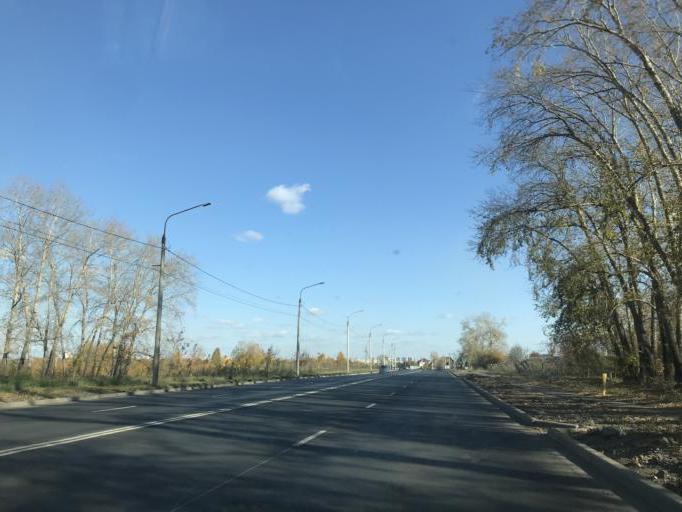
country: RU
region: Chelyabinsk
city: Roshchino
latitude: 55.2400
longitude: 61.3400
